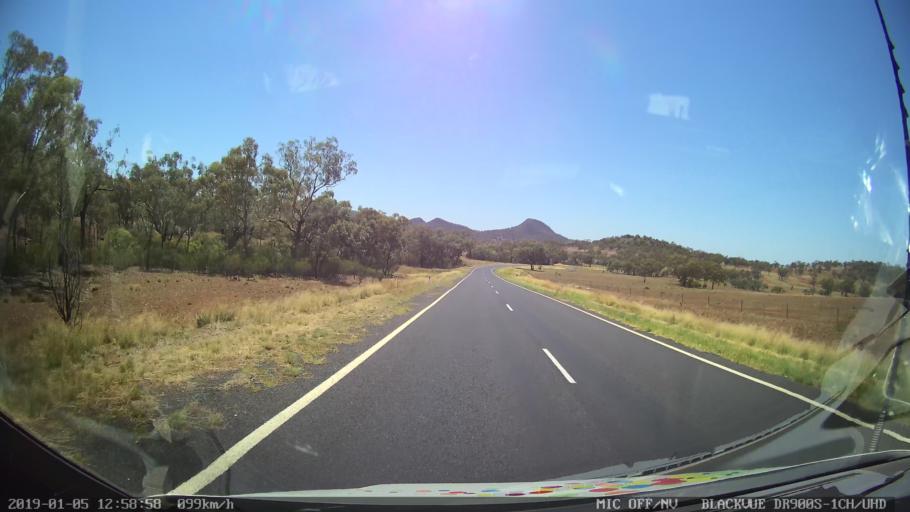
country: AU
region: New South Wales
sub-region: Narrabri
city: Boggabri
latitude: -31.1127
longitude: 149.7582
